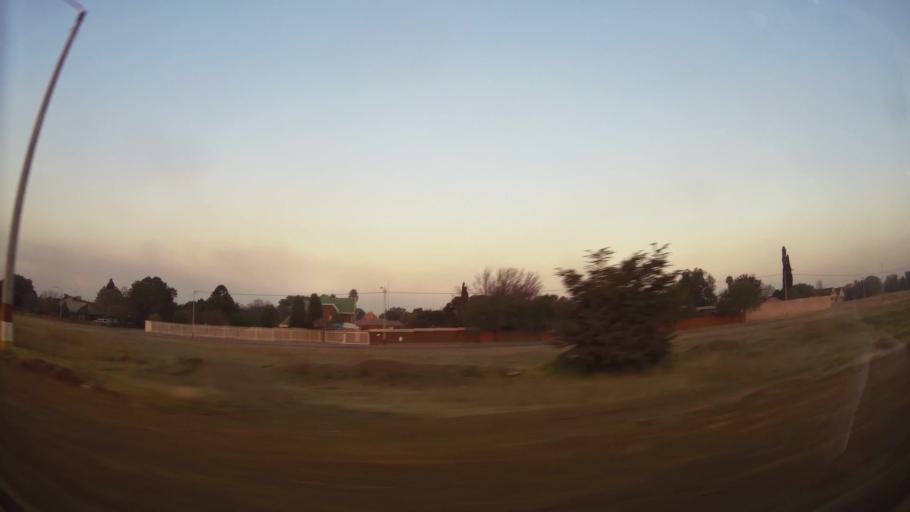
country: ZA
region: Gauteng
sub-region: Ekurhuleni Metropolitan Municipality
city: Springs
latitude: -26.3414
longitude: 28.4184
